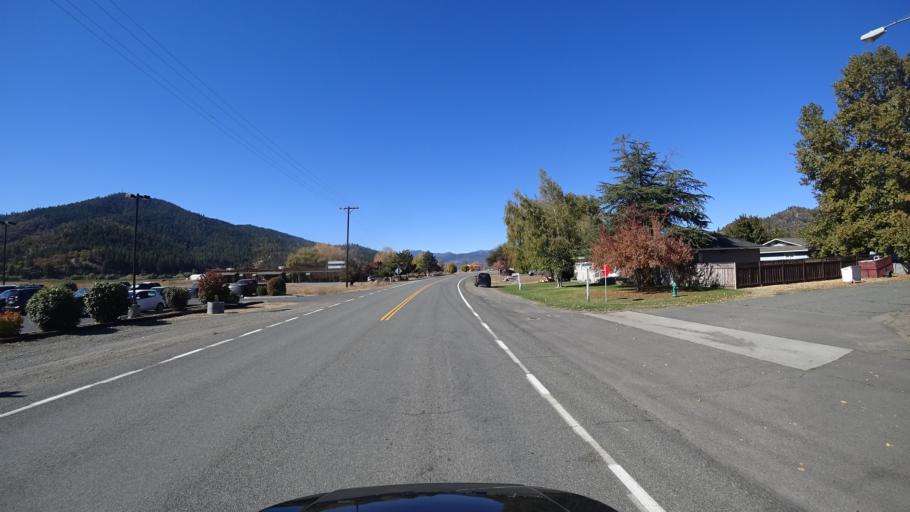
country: US
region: California
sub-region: Siskiyou County
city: Yreka
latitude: 41.6019
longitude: -122.8476
